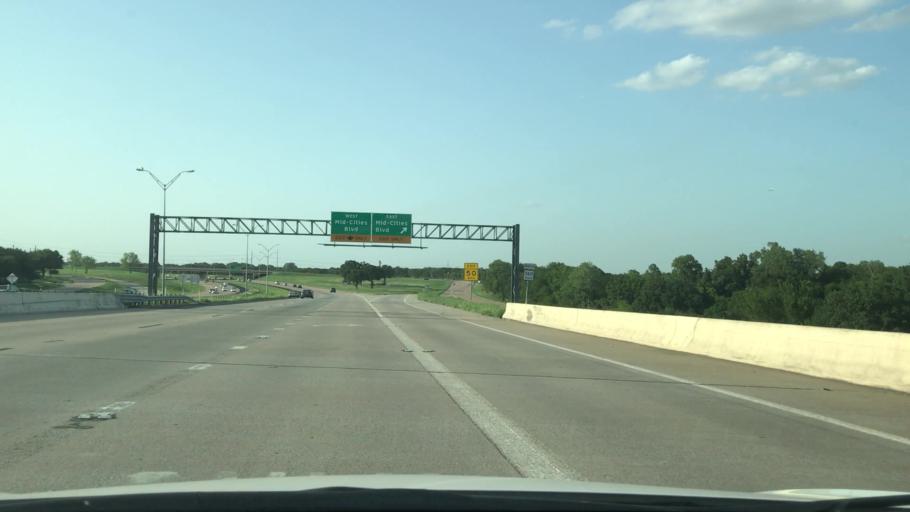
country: US
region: Texas
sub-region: Tarrant County
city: Euless
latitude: 32.8608
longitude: -97.0642
